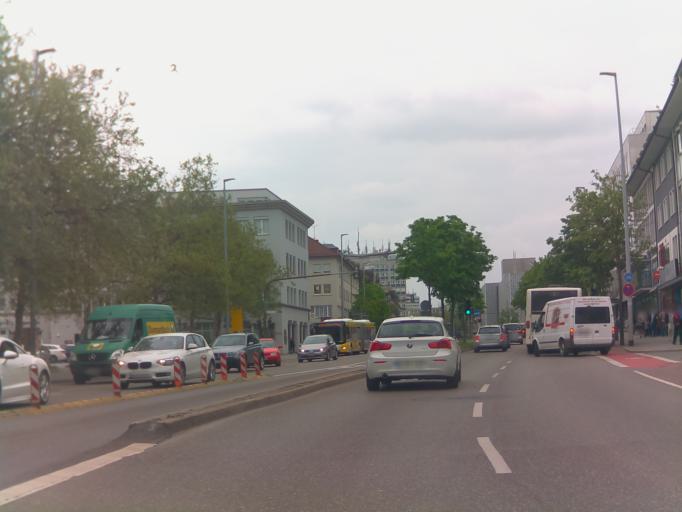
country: DE
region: Baden-Wuerttemberg
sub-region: Tuebingen Region
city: Reutlingen
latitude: 48.4936
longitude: 9.2077
